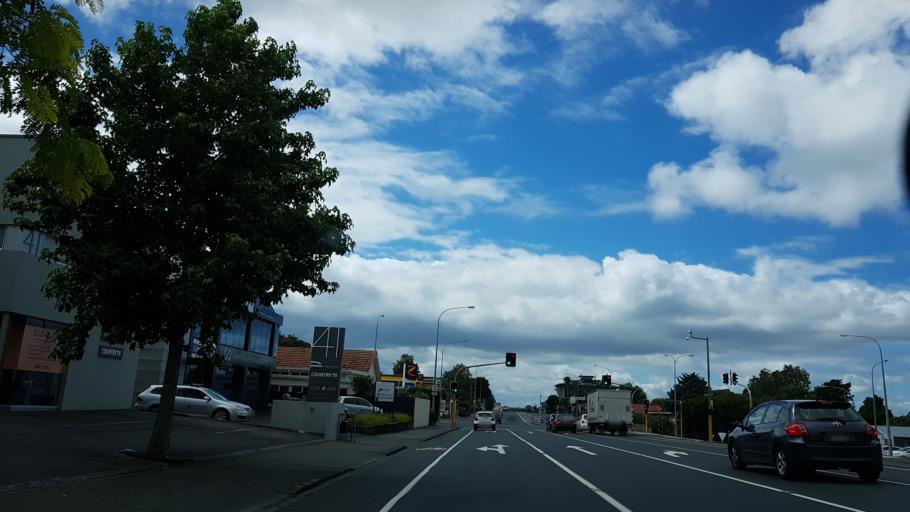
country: NZ
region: Auckland
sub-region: Auckland
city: North Shore
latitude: -36.7849
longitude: 174.7558
